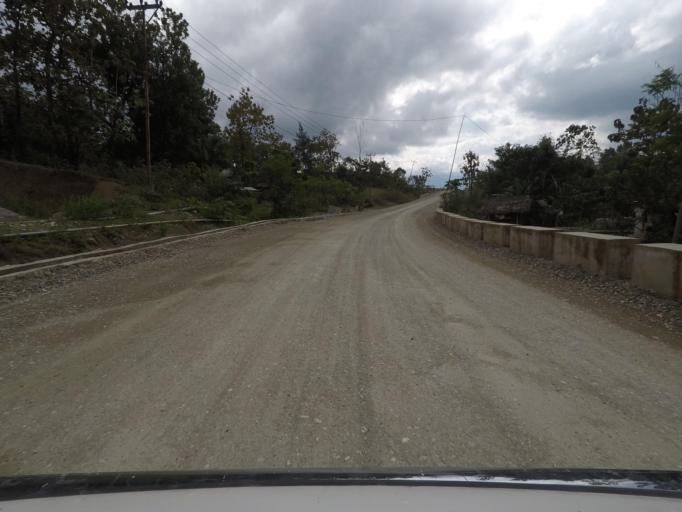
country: TL
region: Viqueque
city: Viqueque
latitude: -8.8019
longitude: 126.3783
